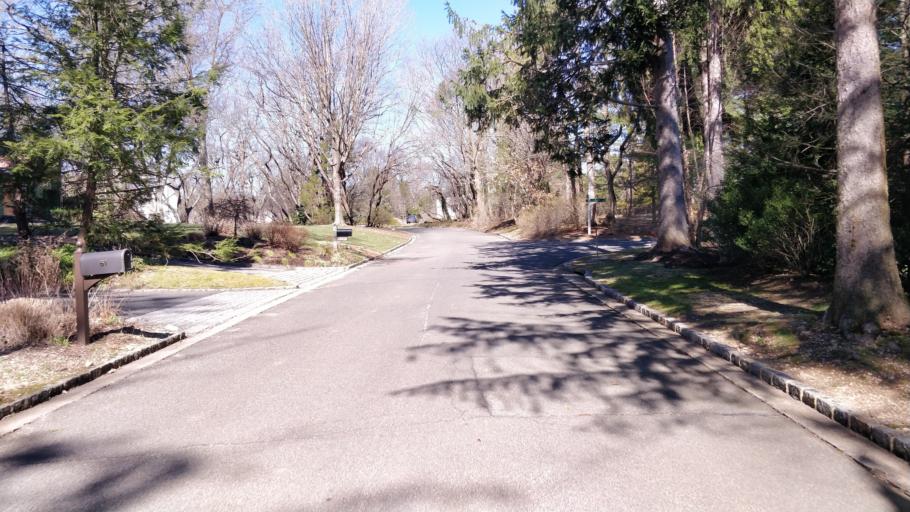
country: US
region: New York
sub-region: Nassau County
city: Syosset
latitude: 40.8326
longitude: -73.5132
